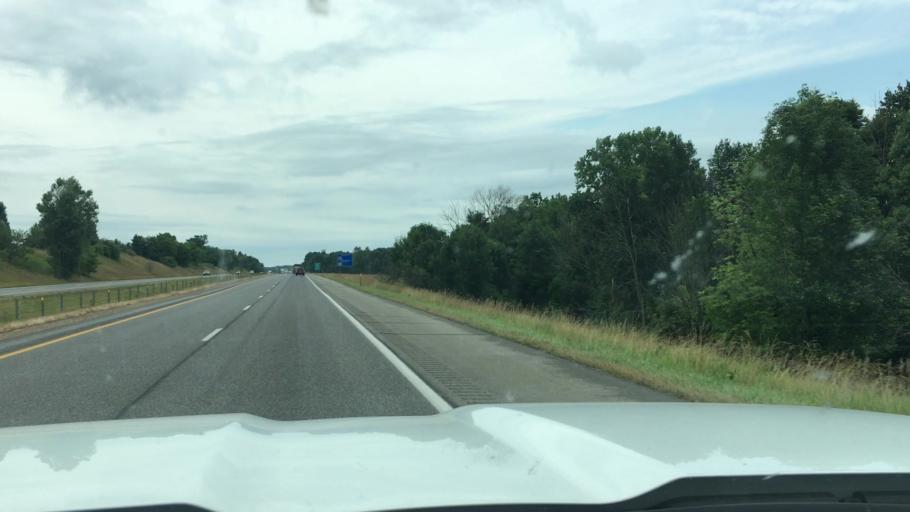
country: US
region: Michigan
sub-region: Allegan County
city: Otsego
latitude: 42.5598
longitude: -85.6625
